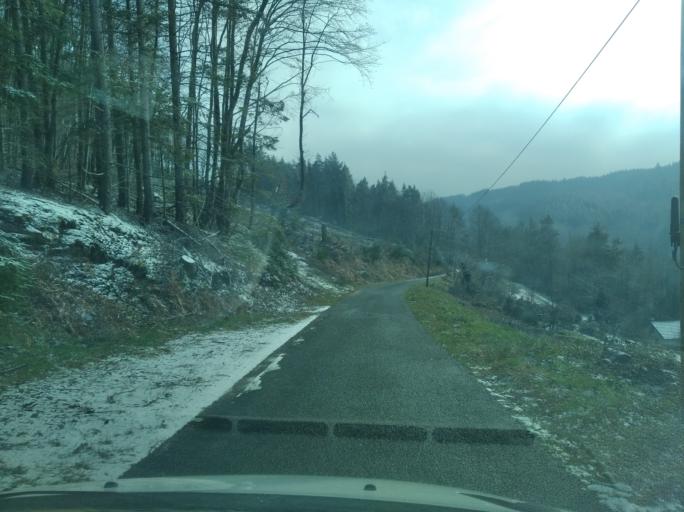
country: FR
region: Rhone-Alpes
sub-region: Departement de la Loire
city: La Pacaudiere
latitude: 46.1357
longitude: 3.7882
